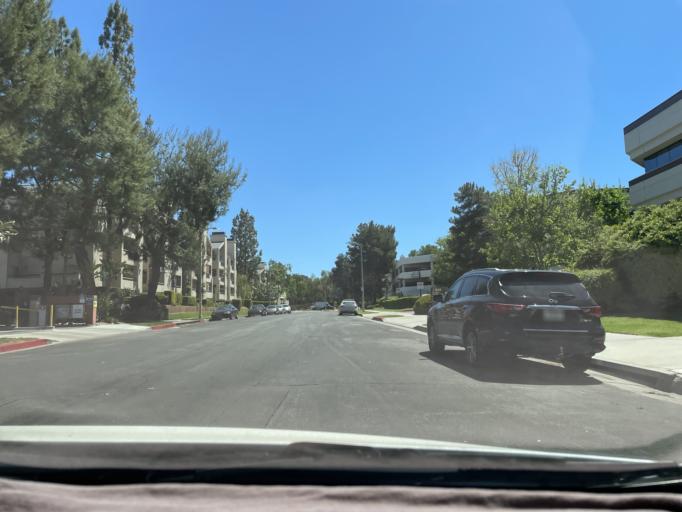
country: US
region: California
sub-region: Los Angeles County
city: Woodland Hills
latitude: 34.1723
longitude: -118.6019
